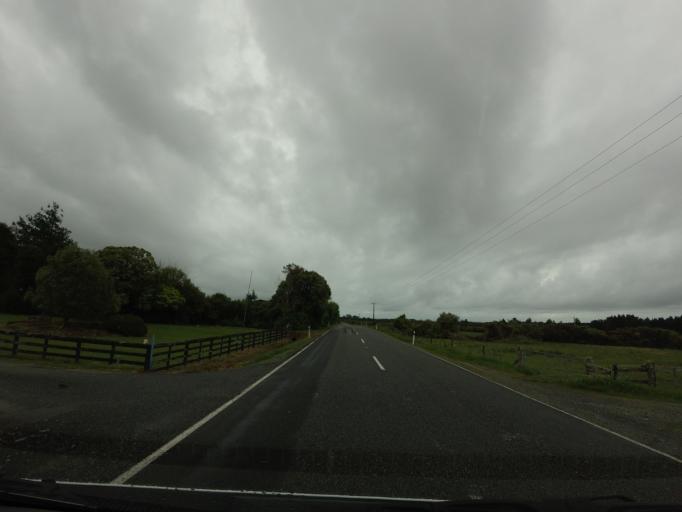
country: NZ
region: West Coast
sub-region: Westland District
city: Hokitika
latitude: -42.8904
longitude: 170.8352
